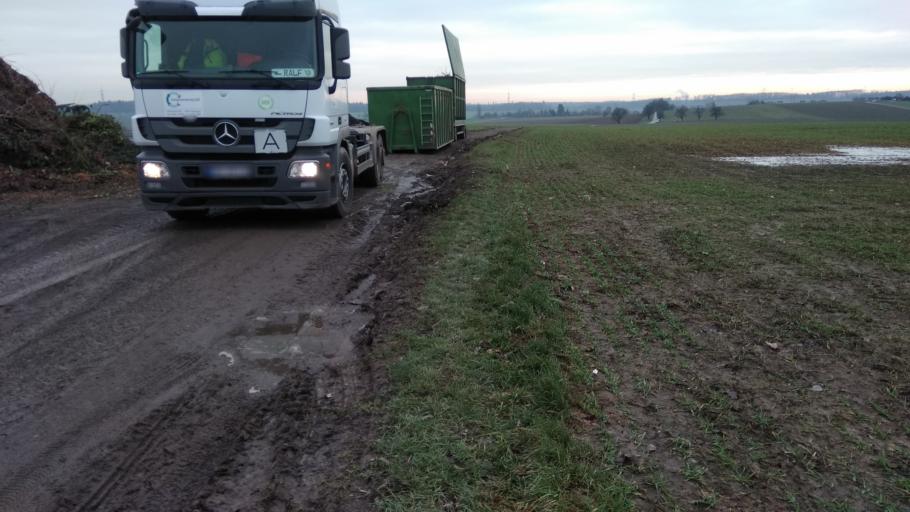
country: DE
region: Baden-Wuerttemberg
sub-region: Karlsruhe Region
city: Mosbach
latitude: 49.3562
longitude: 9.1760
